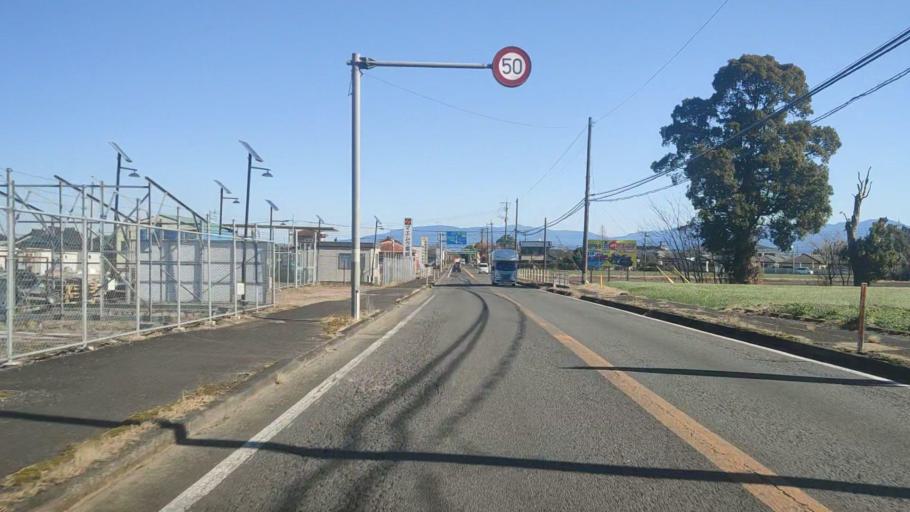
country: JP
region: Kagoshima
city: Sueyoshicho-ninokata
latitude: 31.6977
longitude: 131.0045
